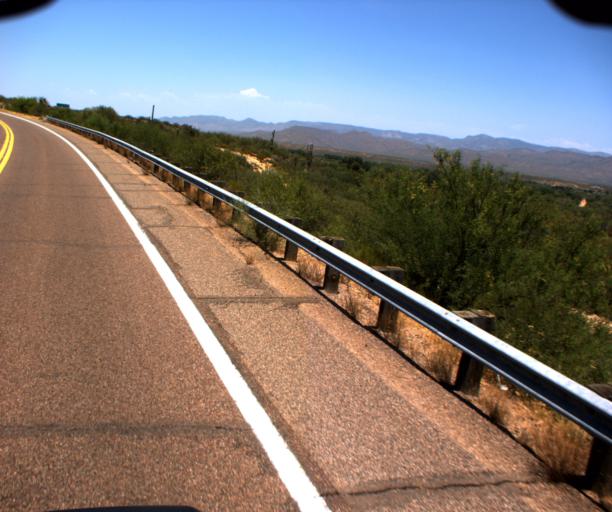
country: US
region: Arizona
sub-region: Gila County
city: Tonto Basin
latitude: 33.7854
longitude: -111.2635
